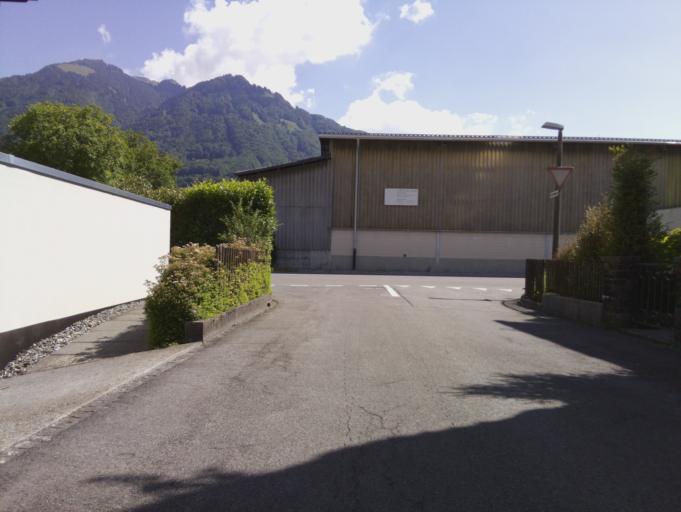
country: CH
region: Glarus
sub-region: Glarus
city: Niederurnen
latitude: 47.1294
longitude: 9.0545
